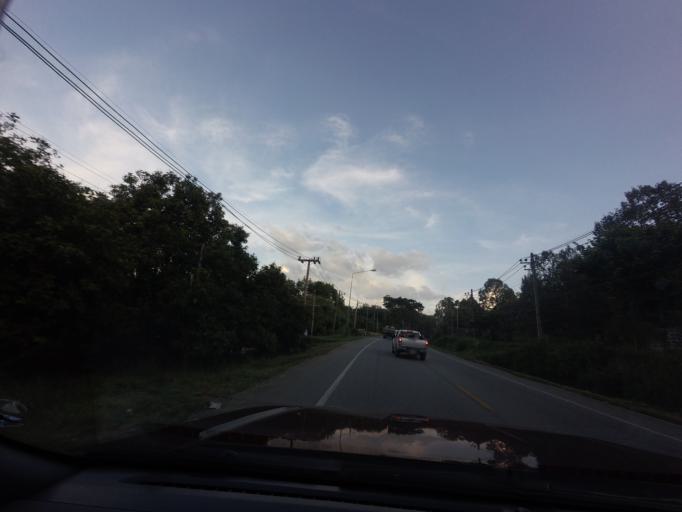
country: TH
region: Yala
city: Than To
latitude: 6.1266
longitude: 101.1922
